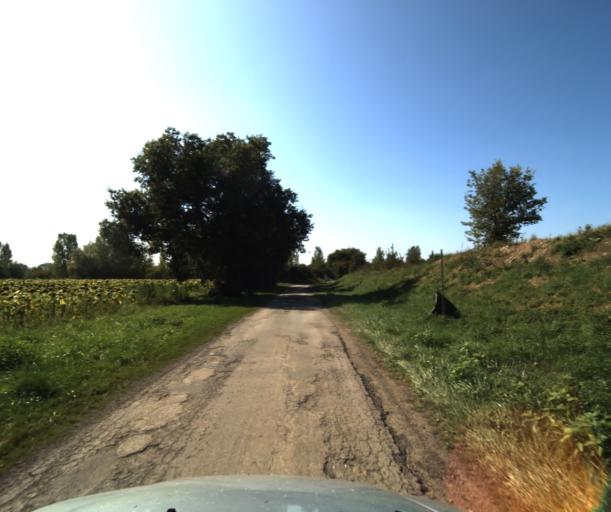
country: FR
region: Midi-Pyrenees
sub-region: Departement de la Haute-Garonne
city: Noe
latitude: 43.3703
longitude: 1.2628
